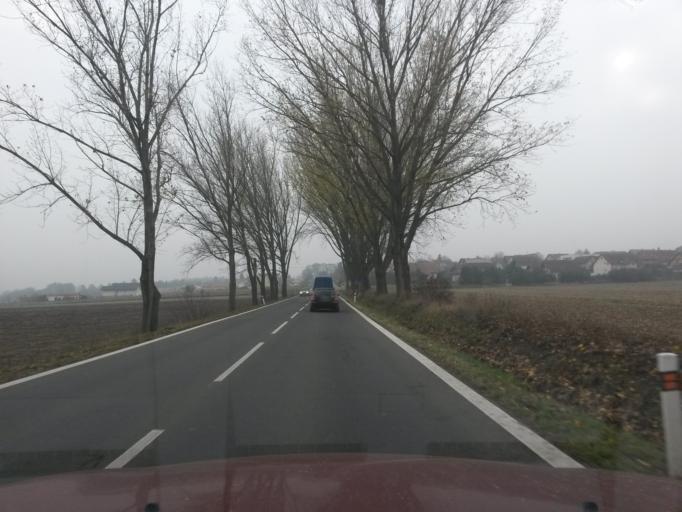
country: SK
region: Kosicky
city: Kosice
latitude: 48.8071
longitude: 21.3015
